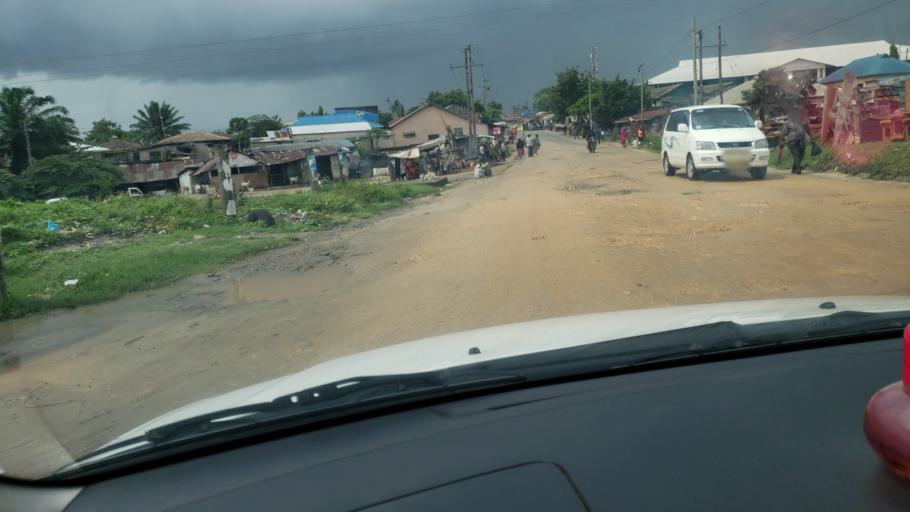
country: TZ
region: Dar es Salaam
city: Magomeni
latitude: -6.8087
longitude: 39.2401
